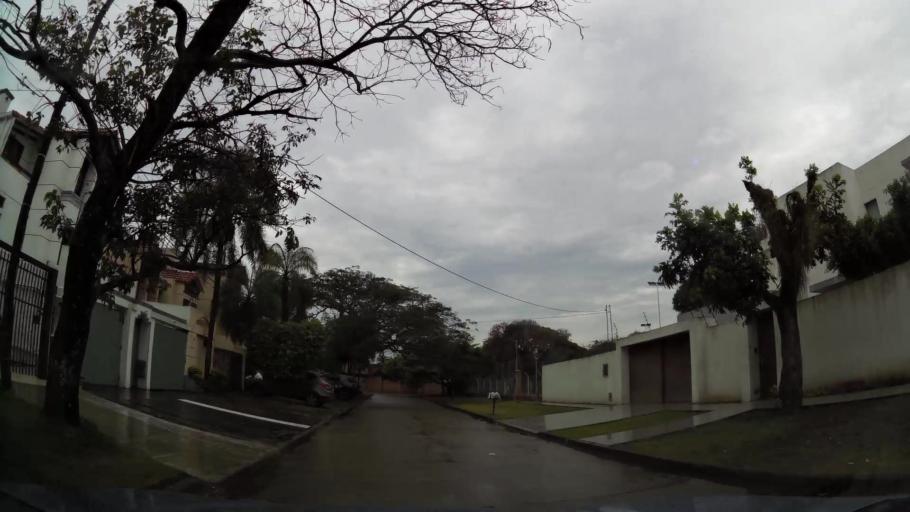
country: BO
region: Santa Cruz
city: Santa Cruz de la Sierra
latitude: -17.8050
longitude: -63.1700
